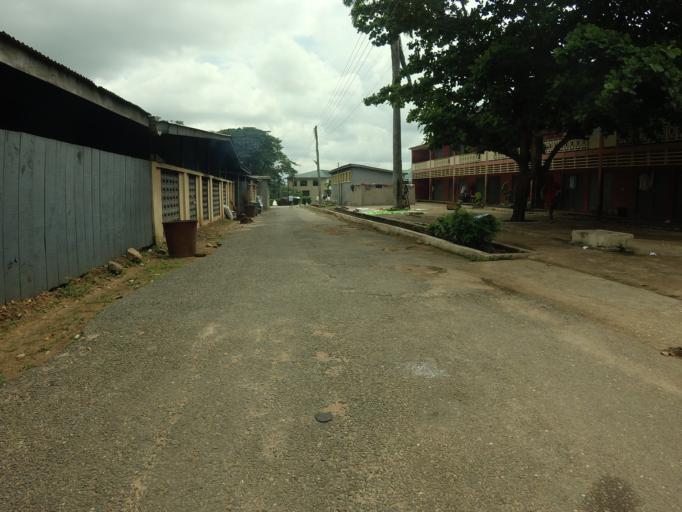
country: GH
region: Volta
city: Ho
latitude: 6.5979
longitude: 0.4749
